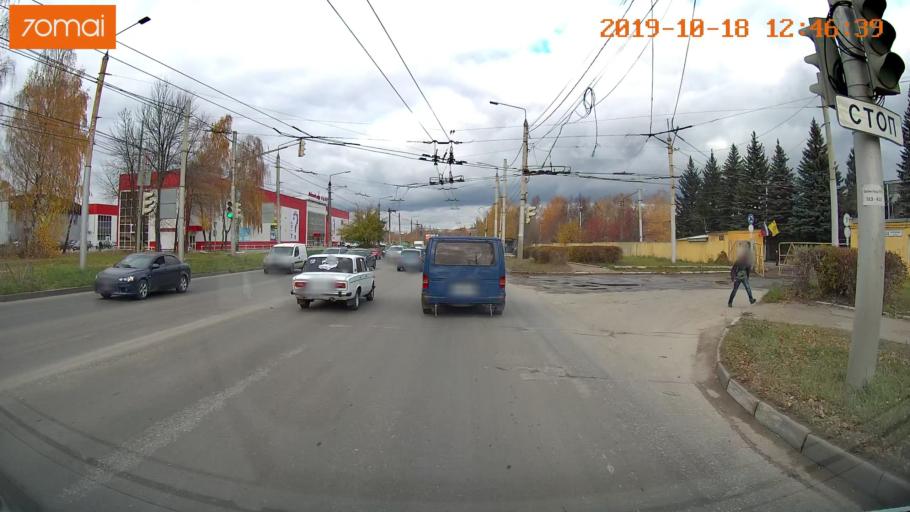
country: RU
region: Rjazan
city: Ryazan'
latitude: 54.6553
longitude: 39.6645
